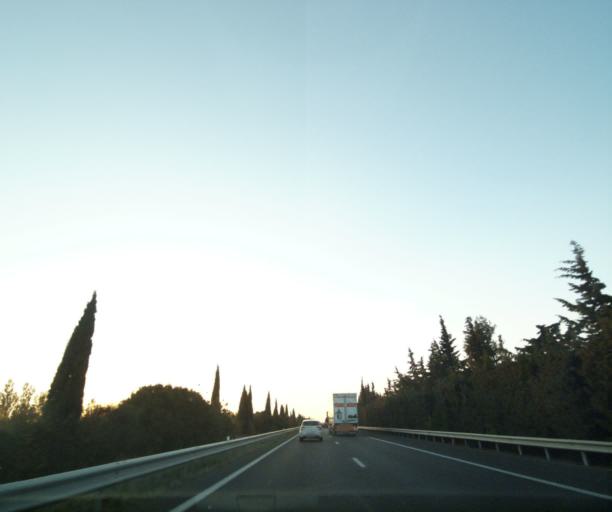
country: FR
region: Provence-Alpes-Cote d'Azur
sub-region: Departement des Bouches-du-Rhone
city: Mouries
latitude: 43.6389
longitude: 4.8941
